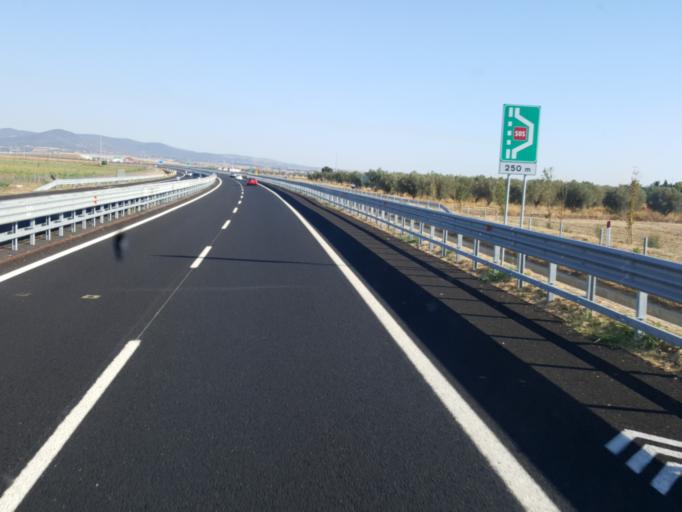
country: IT
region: Latium
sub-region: Provincia di Viterbo
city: Tarquinia
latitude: 42.2196
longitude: 11.7717
